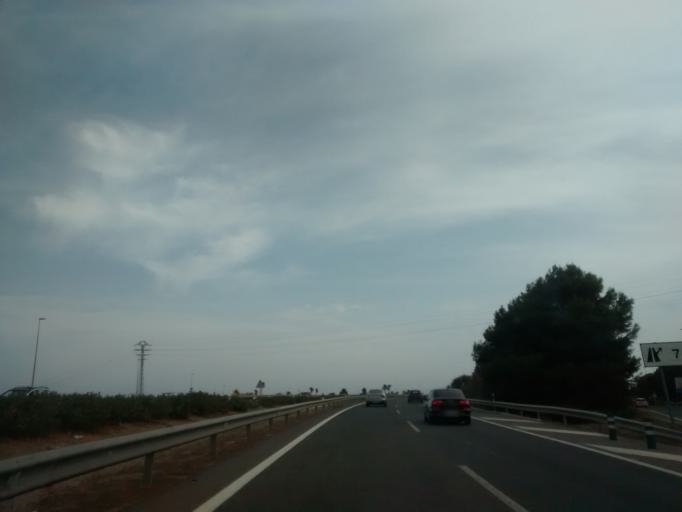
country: ES
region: Murcia
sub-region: Murcia
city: San Javier
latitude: 37.7917
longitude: -0.8390
